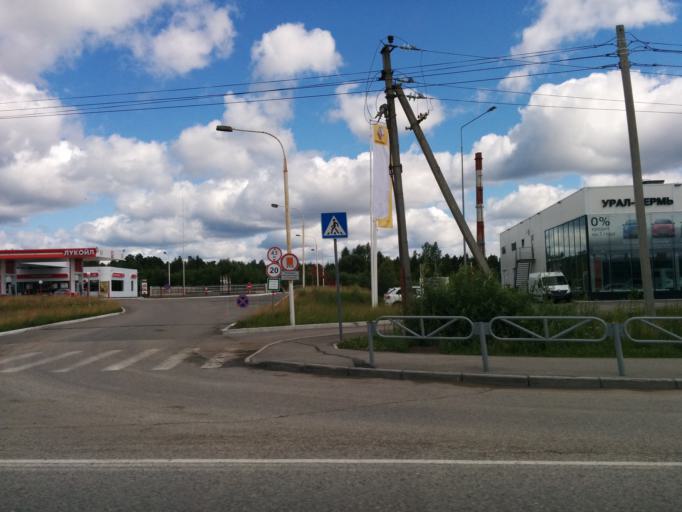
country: RU
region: Perm
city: Perm
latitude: 58.0364
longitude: 56.1967
